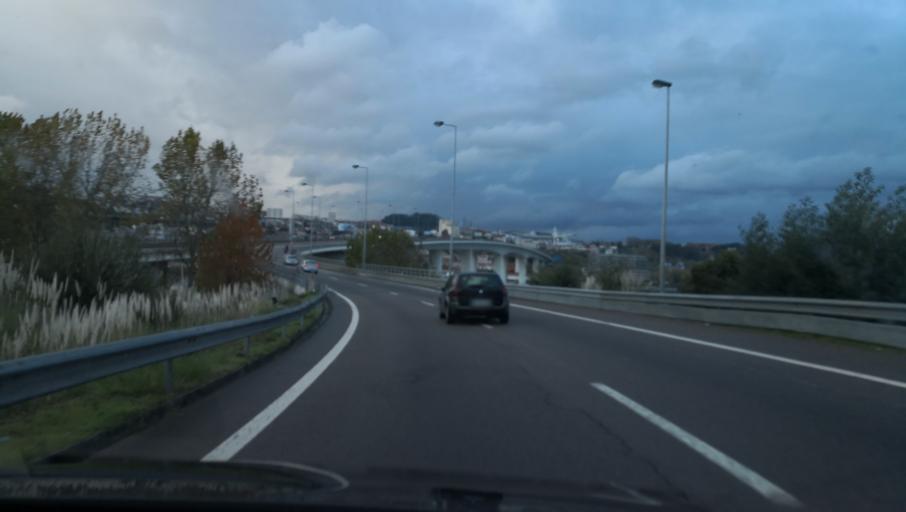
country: PT
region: Porto
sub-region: Vila Nova de Gaia
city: Oliveira do Douro
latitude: 41.1372
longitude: -8.5797
